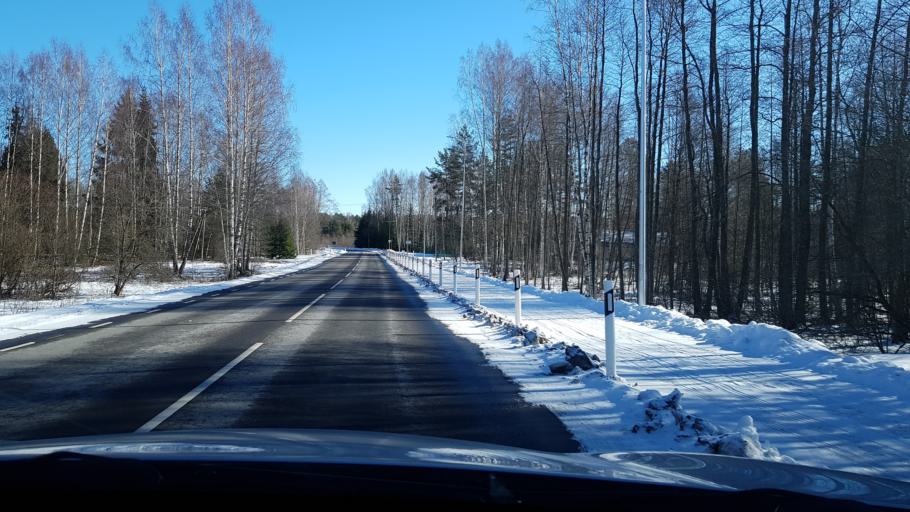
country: RU
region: Pskov
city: Pechory
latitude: 57.9581
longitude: 27.6206
